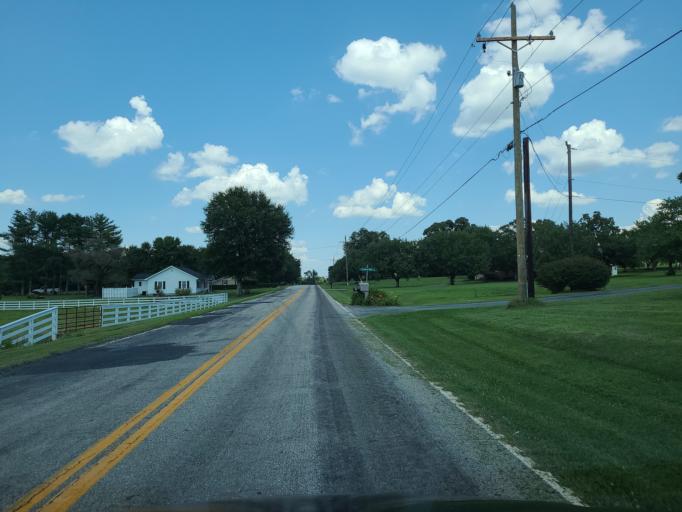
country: US
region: South Carolina
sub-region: Spartanburg County
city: Inman Mills
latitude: 35.0359
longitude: -82.1499
